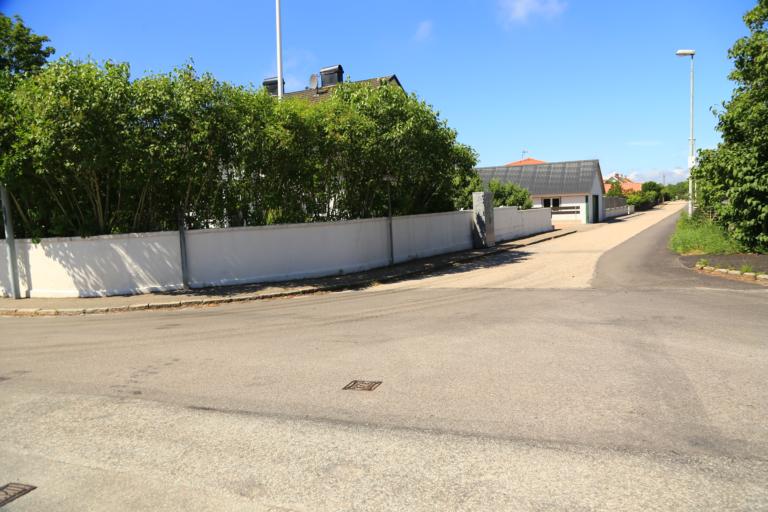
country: SE
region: Halland
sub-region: Varbergs Kommun
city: Varberg
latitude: 57.1017
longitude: 12.2793
